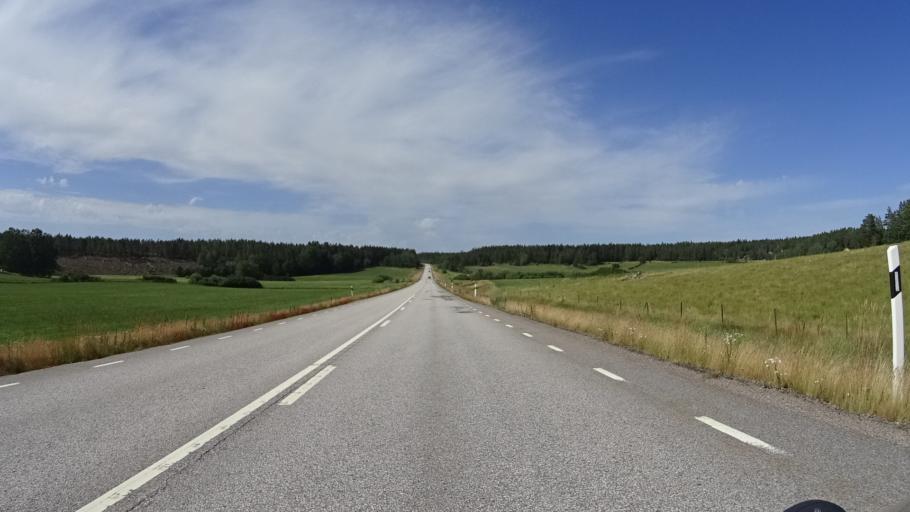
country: SE
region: Kalmar
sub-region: Vasterviks Kommun
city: Gamleby
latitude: 57.9439
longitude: 16.3837
